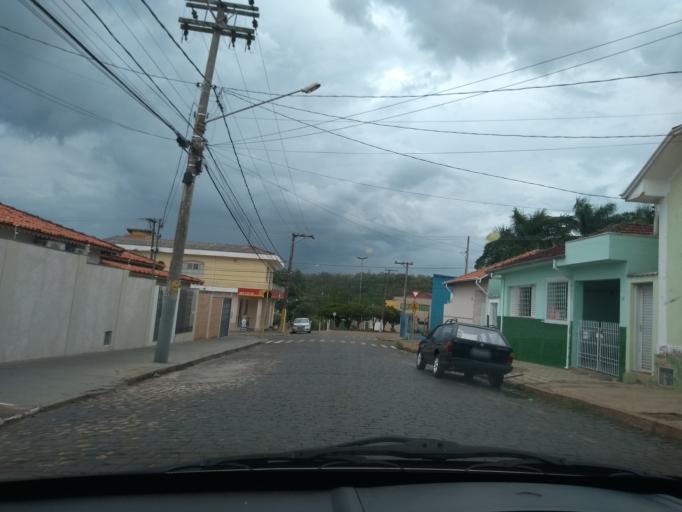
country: BR
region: Sao Paulo
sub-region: Casa Branca
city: Casa Branca
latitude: -21.7755
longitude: -47.0804
